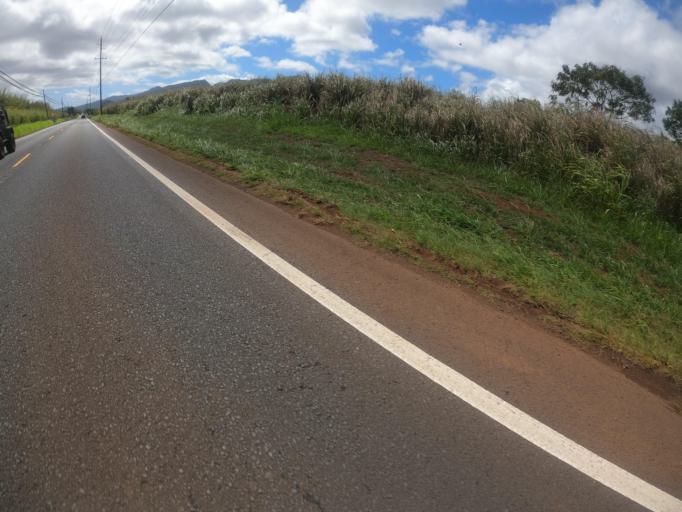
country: US
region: Hawaii
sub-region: Honolulu County
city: Schofield Barracks
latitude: 21.4686
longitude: -158.0538
